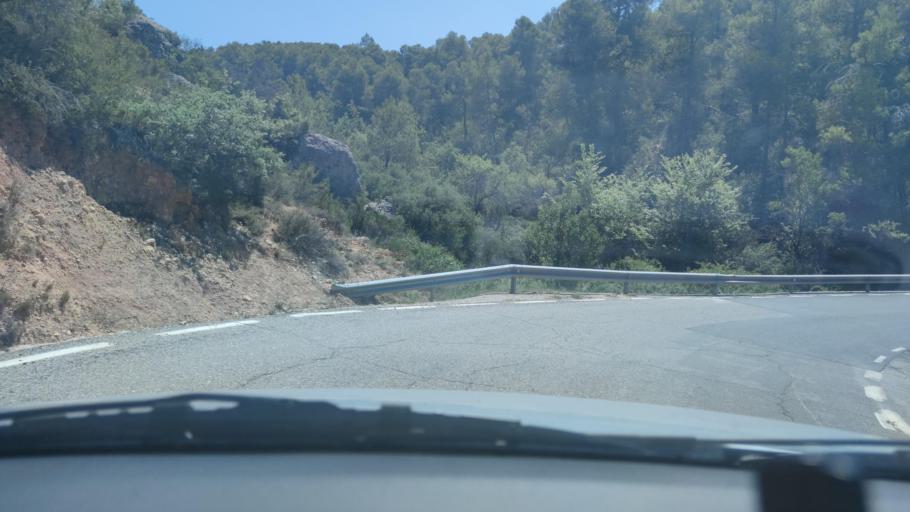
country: ES
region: Catalonia
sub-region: Provincia de Tarragona
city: Vilanova de Prades
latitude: 41.3773
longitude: 0.9400
